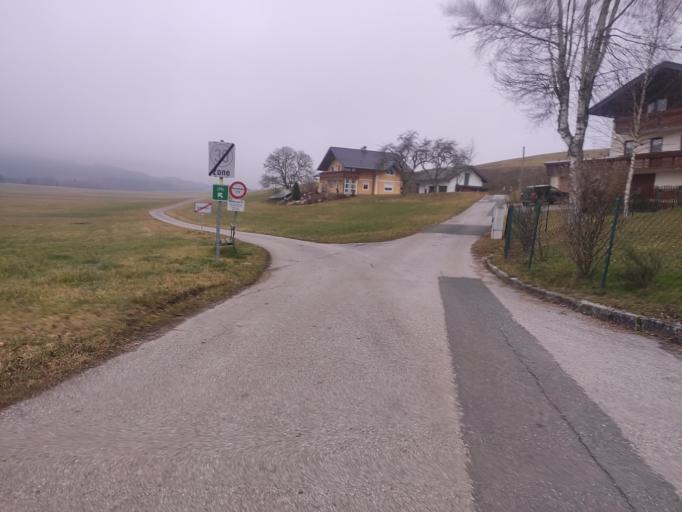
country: AT
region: Salzburg
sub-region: Politischer Bezirk Salzburg-Umgebung
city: Schleedorf
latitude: 47.9557
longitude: 13.1474
